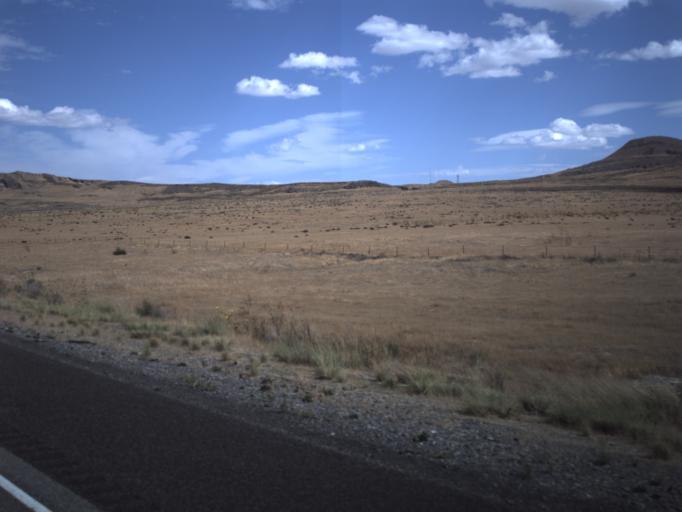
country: US
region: Utah
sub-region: Tooele County
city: Grantsville
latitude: 40.7986
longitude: -112.9448
